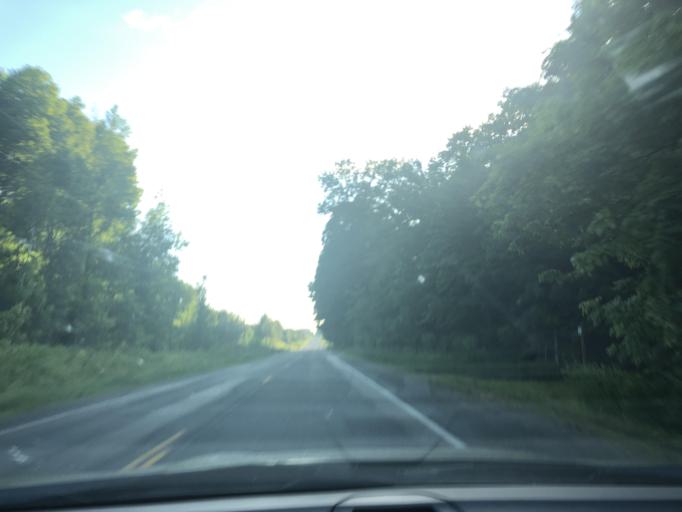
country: US
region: Michigan
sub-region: Missaukee County
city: Lake City
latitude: 44.4665
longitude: -85.0815
